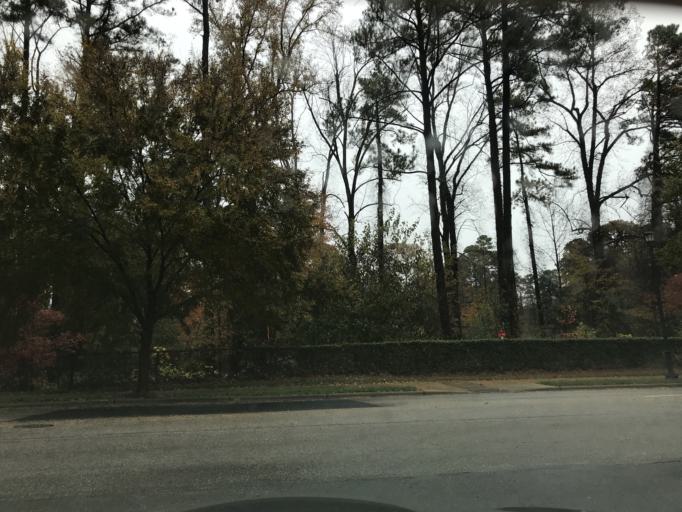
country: US
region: North Carolina
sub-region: Wake County
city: West Raleigh
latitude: 35.8368
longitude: -78.6359
